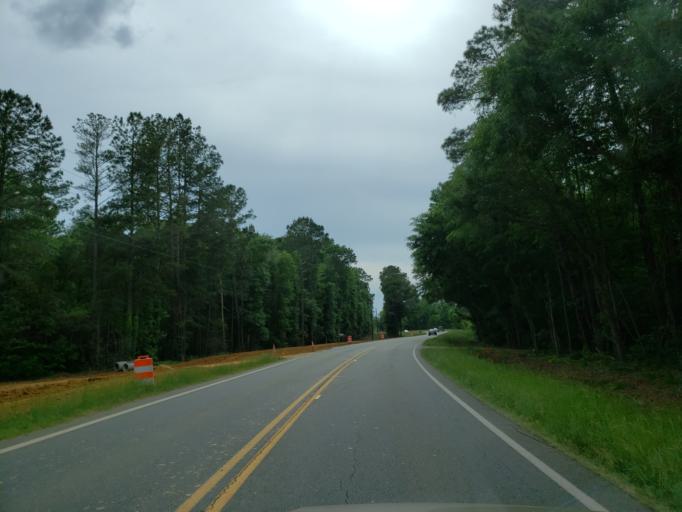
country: US
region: Georgia
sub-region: Macon County
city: Marshallville
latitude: 32.3798
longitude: -83.8829
